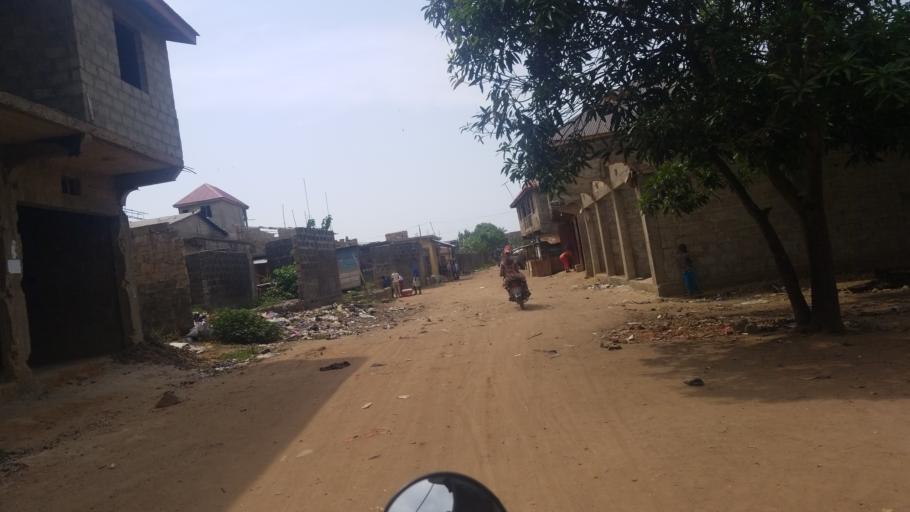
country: SL
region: Western Area
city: Waterloo
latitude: 8.3285
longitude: -13.0488
